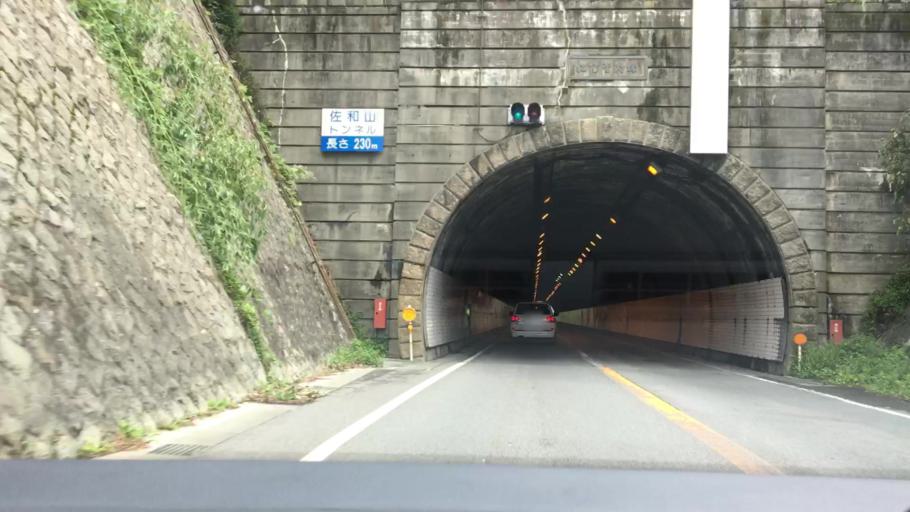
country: JP
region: Shiga Prefecture
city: Hikone
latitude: 35.2755
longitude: 136.2700
